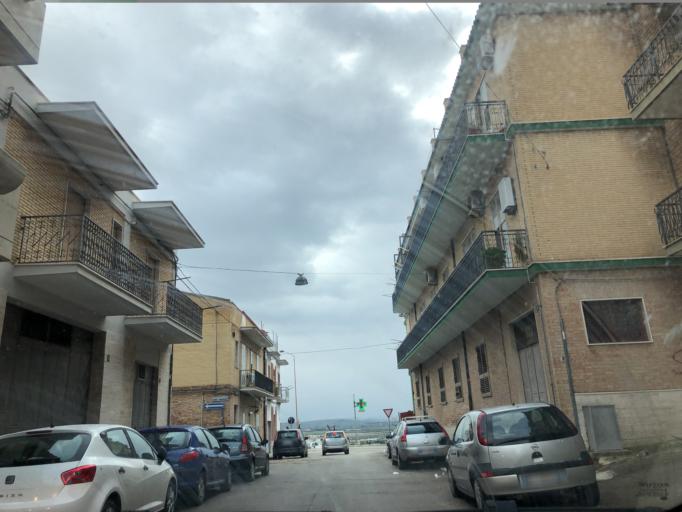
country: IT
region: Apulia
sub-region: Provincia di Foggia
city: Lucera
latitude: 41.5042
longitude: 15.3386
